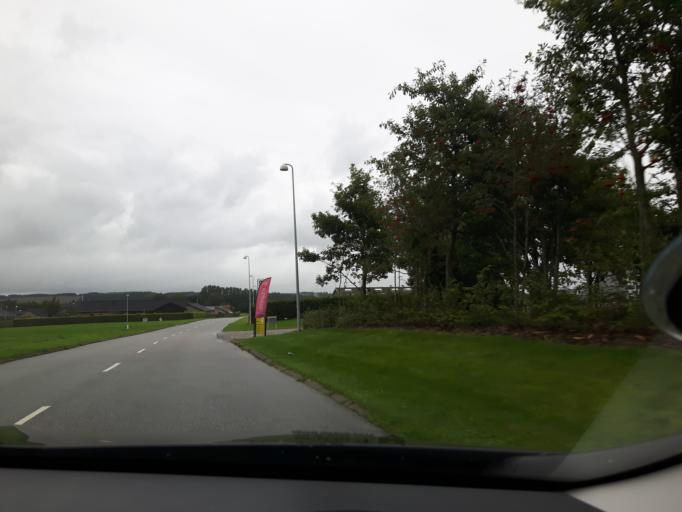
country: DK
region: Central Jutland
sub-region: Skanderborg Kommune
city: Ry
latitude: 56.1526
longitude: 9.8163
